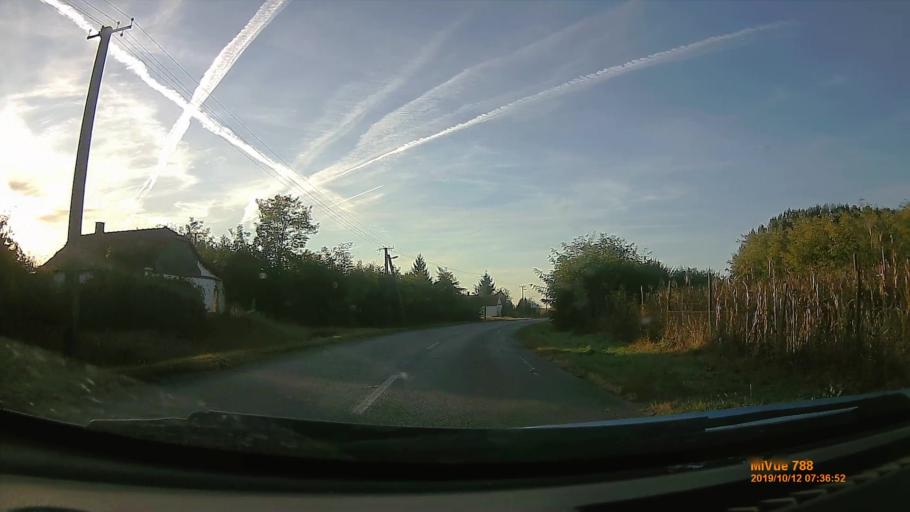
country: HU
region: Hajdu-Bihar
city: Pocsaj
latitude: 47.2422
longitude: 21.8146
